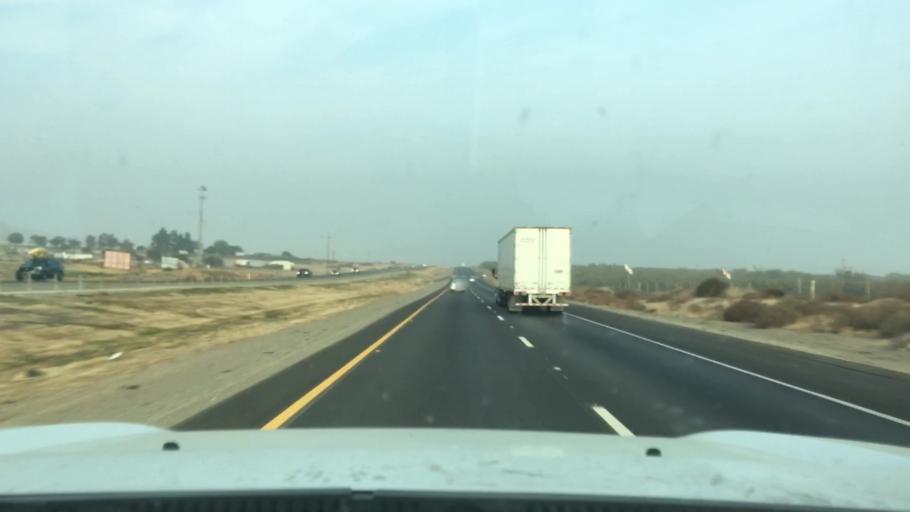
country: US
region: California
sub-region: Stanislaus County
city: Patterson
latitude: 37.5634
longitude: -121.2976
